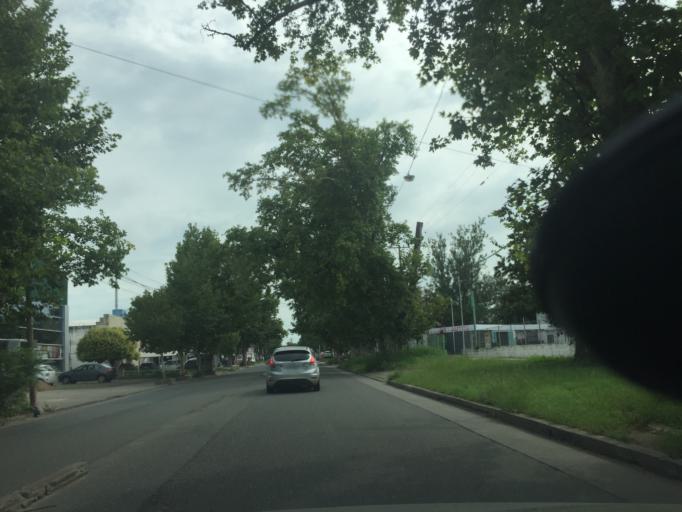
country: AR
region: Cordoba
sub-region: Departamento de Capital
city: Cordoba
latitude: -31.4534
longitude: -64.2059
